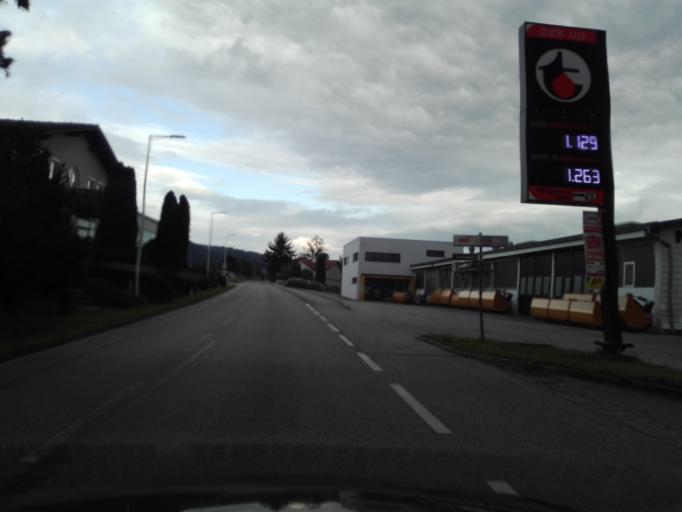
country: AT
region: Upper Austria
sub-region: Politischer Bezirk Braunau am Inn
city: Altheim
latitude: 48.2392
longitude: 13.3491
